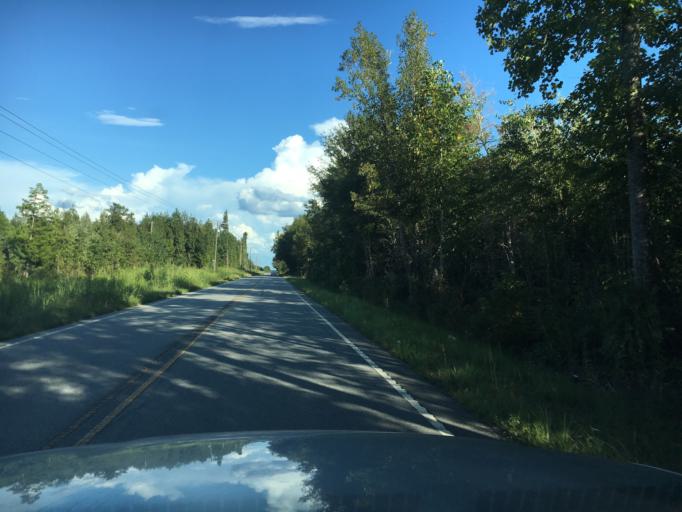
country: US
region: South Carolina
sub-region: Greenville County
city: Five Forks
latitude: 34.7988
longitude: -82.1505
